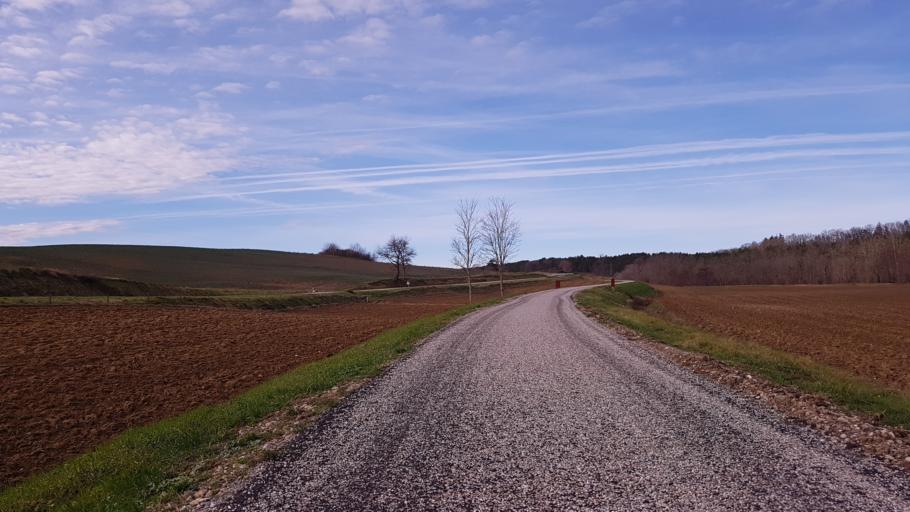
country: FR
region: Languedoc-Roussillon
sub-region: Departement de l'Aude
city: Chalabre
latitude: 42.9527
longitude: 1.9868
